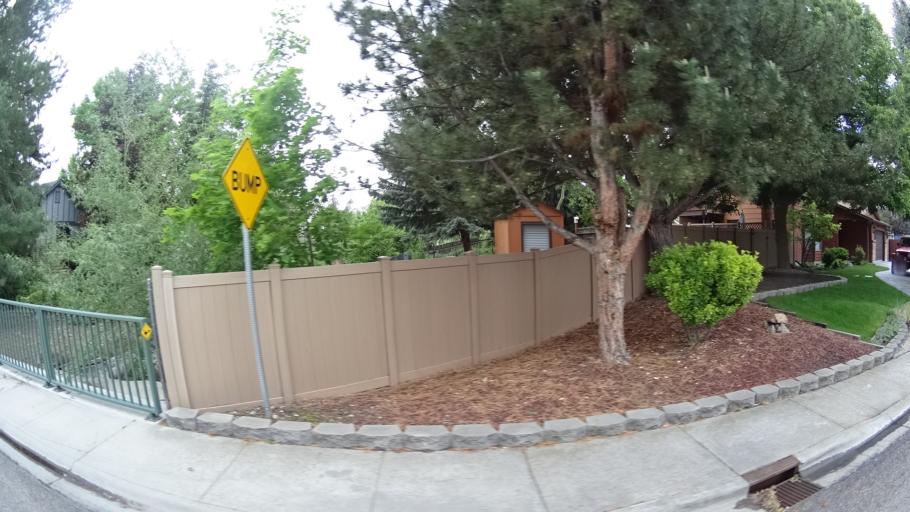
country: US
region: Idaho
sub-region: Ada County
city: Garden City
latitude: 43.6782
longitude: -116.2742
